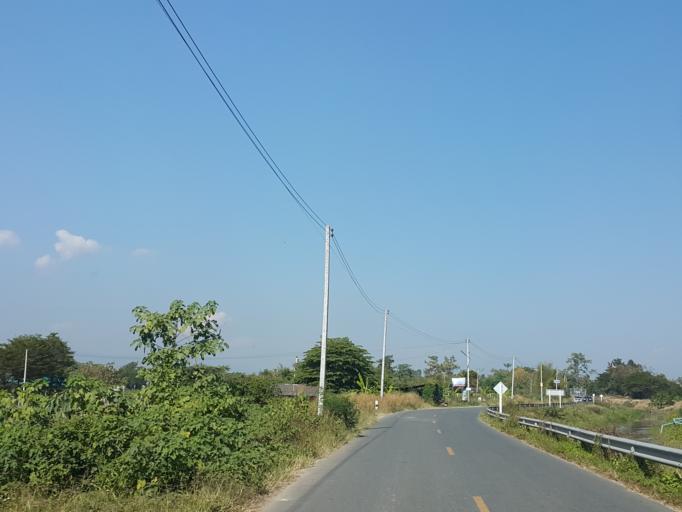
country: TH
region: Chiang Mai
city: San Sai
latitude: 18.9440
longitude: 98.9929
